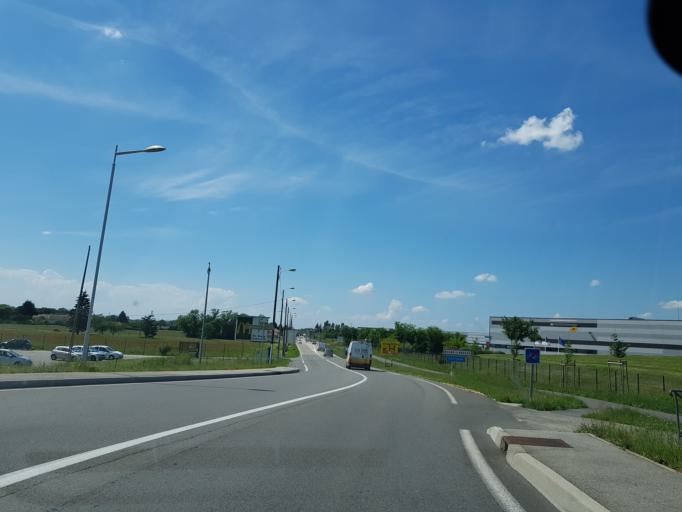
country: FR
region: Rhone-Alpes
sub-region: Departement de l'Ain
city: Montagnat
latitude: 46.1953
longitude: 5.2693
